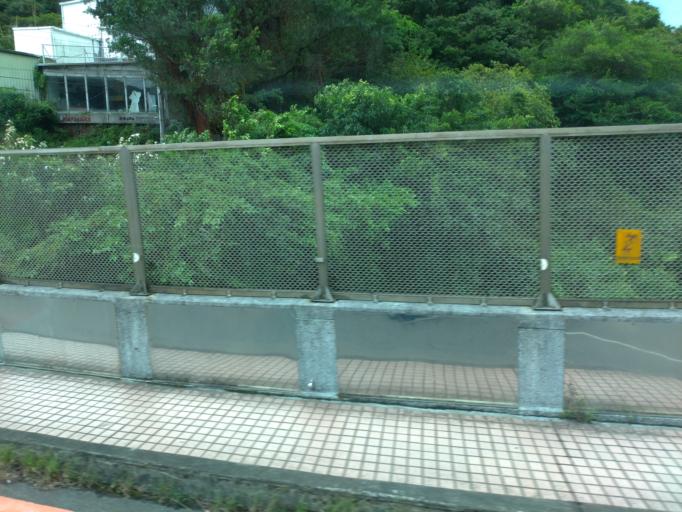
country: TW
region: Taiwan
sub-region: Keelung
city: Keelung
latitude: 25.1019
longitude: 121.7451
